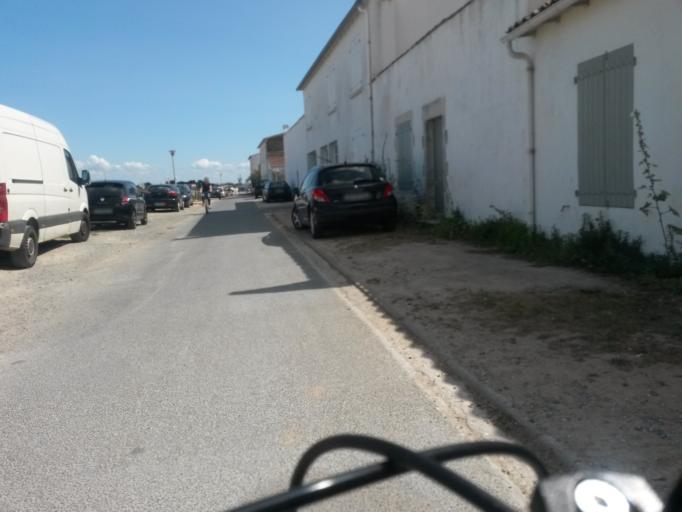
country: FR
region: Poitou-Charentes
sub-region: Departement de la Charente-Maritime
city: Rivedoux-Plage
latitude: 46.1637
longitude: -1.2804
